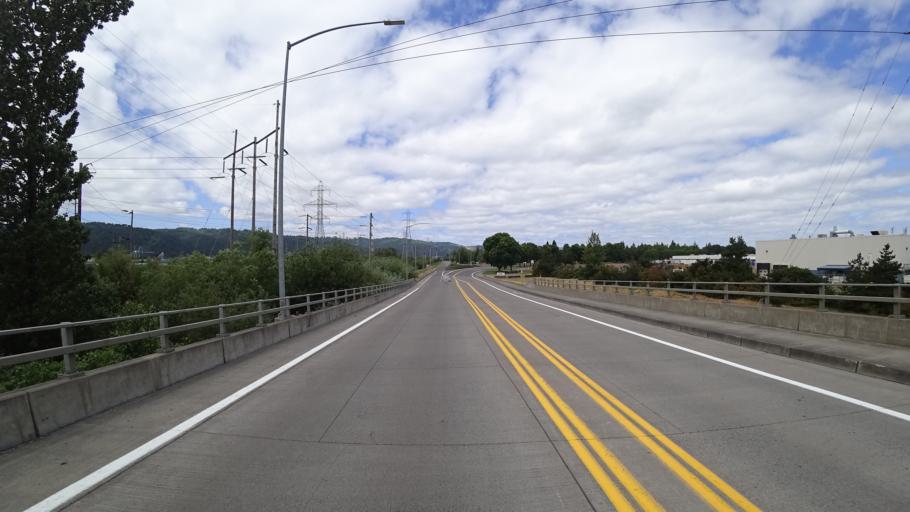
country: US
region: Oregon
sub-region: Washington County
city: West Haven
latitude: 45.6169
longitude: -122.7673
